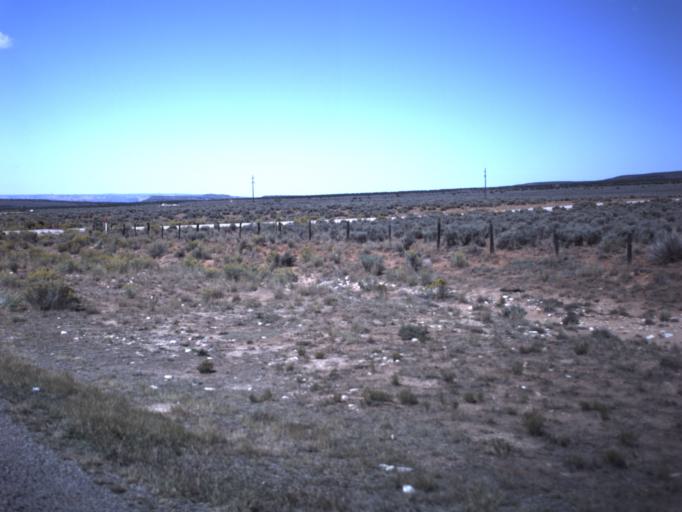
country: US
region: Utah
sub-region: Grand County
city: Moab
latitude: 38.3094
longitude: -109.2931
